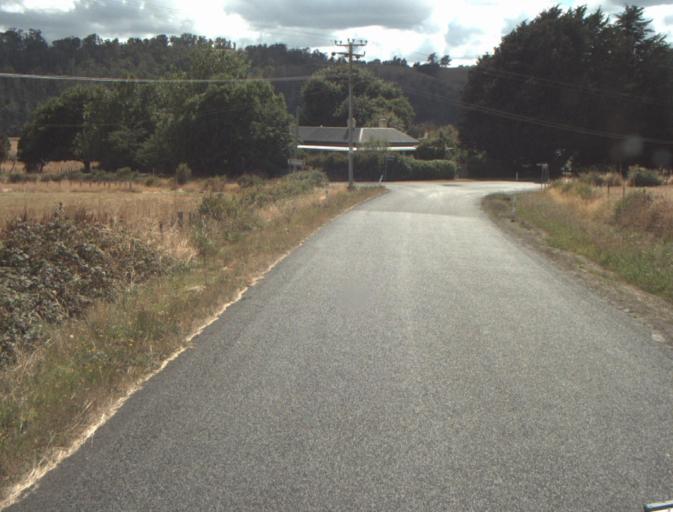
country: AU
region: Tasmania
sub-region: Launceston
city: Mayfield
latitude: -41.2371
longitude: 147.1492
